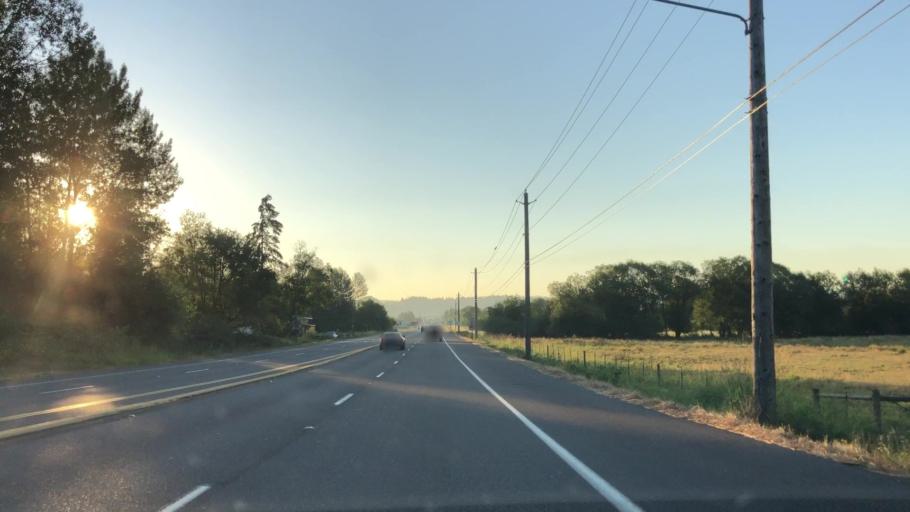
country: US
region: Washington
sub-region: King County
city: Lakeland North
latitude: 47.3536
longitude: -122.2626
